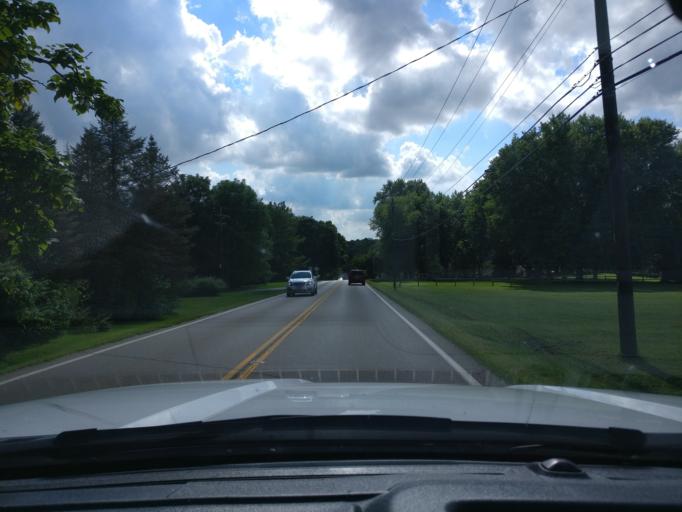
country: US
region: Ohio
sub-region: Warren County
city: Five Points
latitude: 39.5248
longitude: -84.1781
